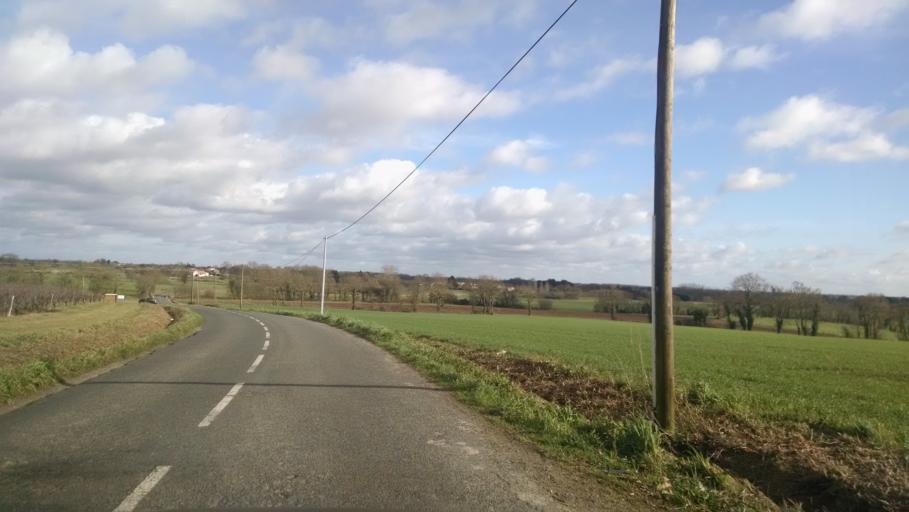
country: FR
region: Pays de la Loire
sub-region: Departement de la Loire-Atlantique
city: Remouille
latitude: 47.0574
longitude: -1.3519
